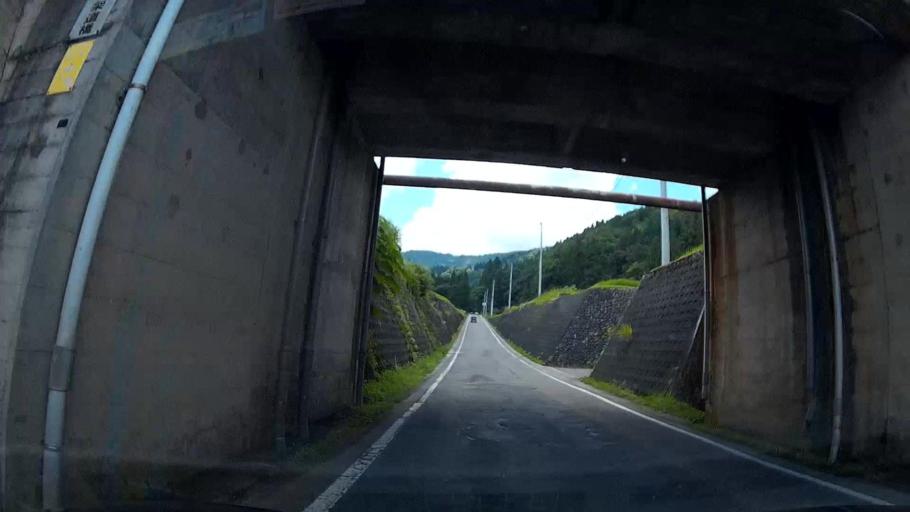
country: JP
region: Niigata
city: Shiozawa
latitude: 37.0183
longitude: 138.8195
